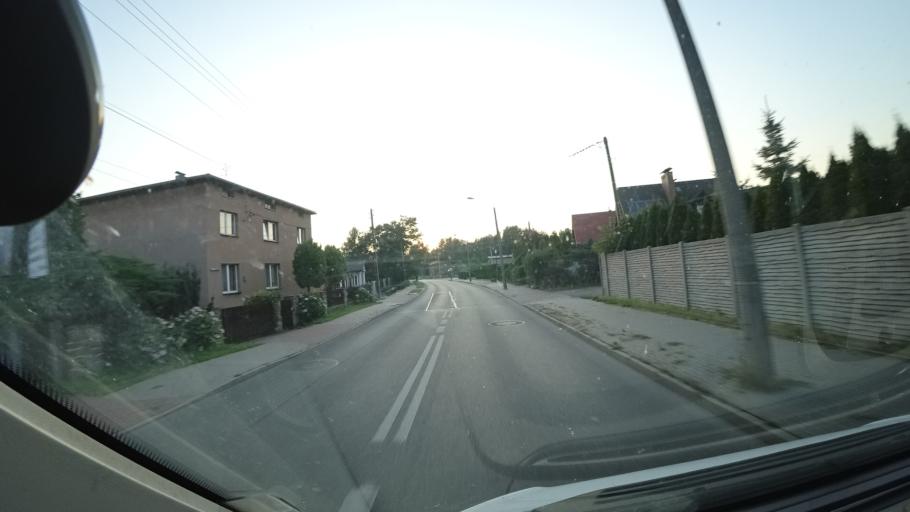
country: PL
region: Silesian Voivodeship
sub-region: Zabrze
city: Zabrze
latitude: 50.2807
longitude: 18.8022
